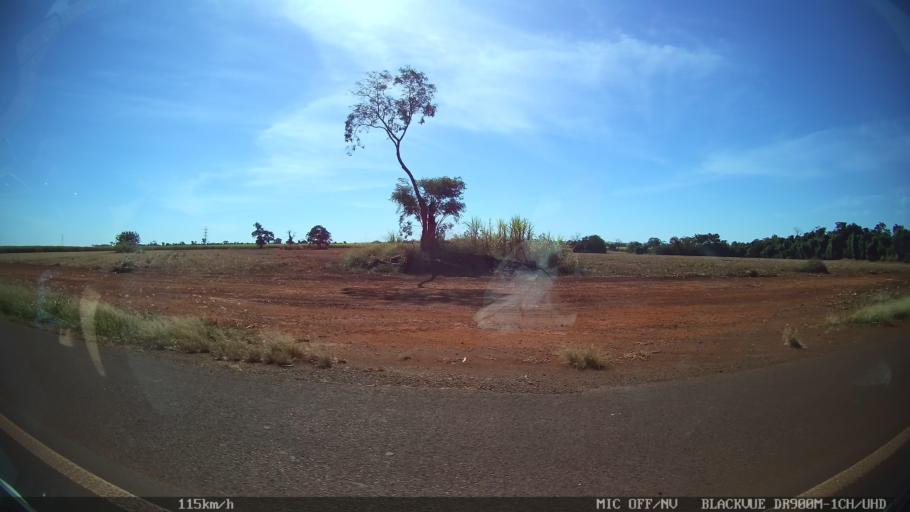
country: BR
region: Sao Paulo
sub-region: Guaira
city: Guaira
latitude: -20.4434
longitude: -48.3352
